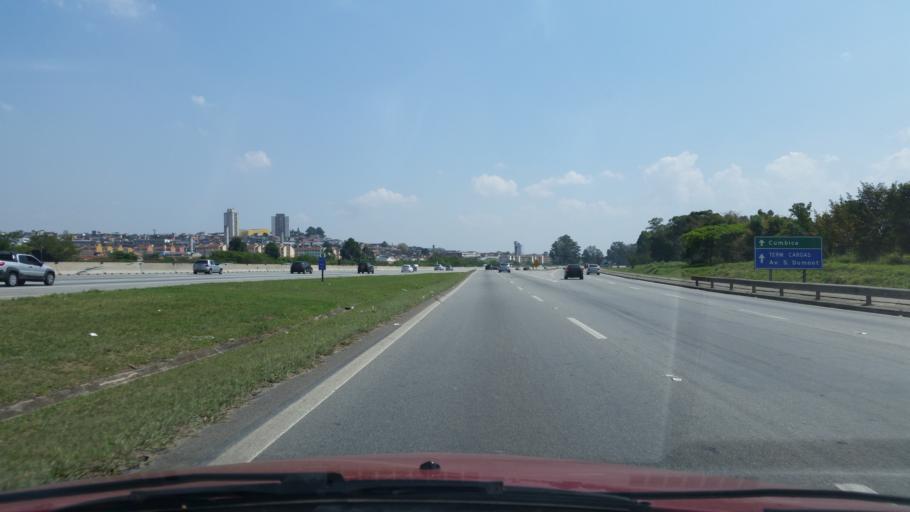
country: BR
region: Sao Paulo
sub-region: Guarulhos
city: Guarulhos
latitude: -23.4817
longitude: -46.4587
